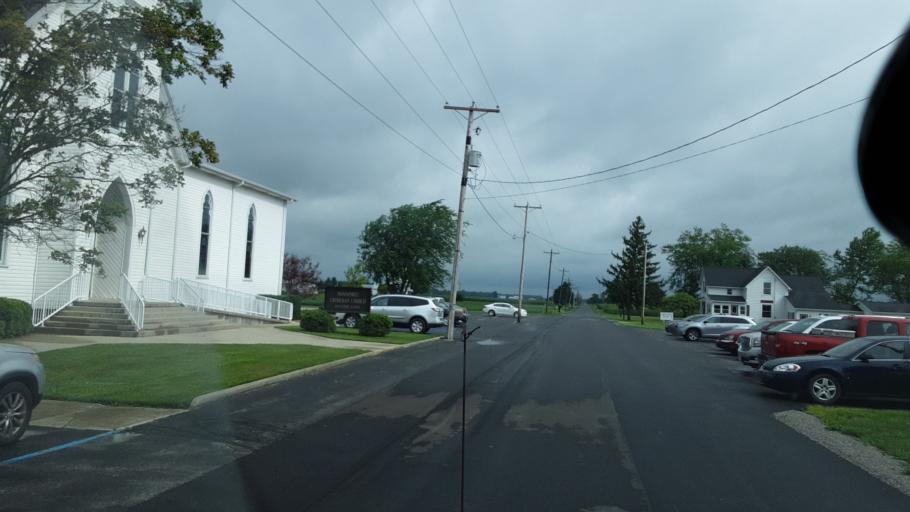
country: US
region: Indiana
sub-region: Adams County
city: Decatur
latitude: 40.8697
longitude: -84.8427
